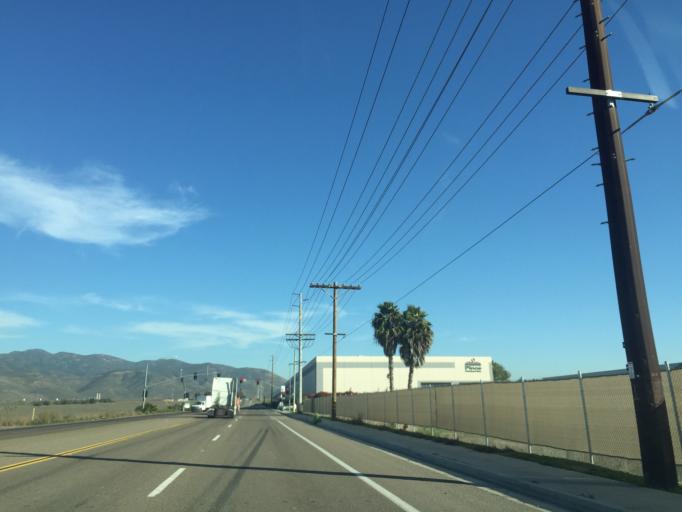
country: MX
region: Baja California
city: Tijuana
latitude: 32.5675
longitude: -116.9423
